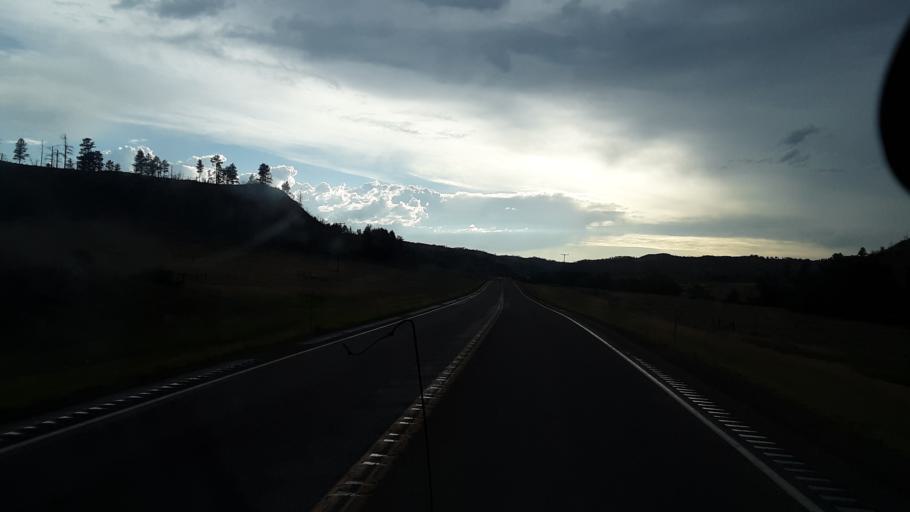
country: US
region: Montana
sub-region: Rosebud County
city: Lame Deer
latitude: 45.6180
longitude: -106.3916
